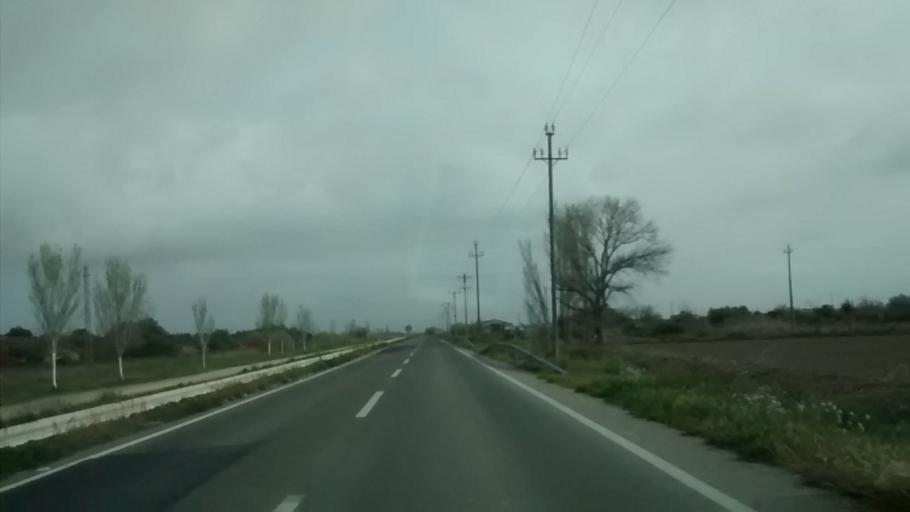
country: ES
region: Catalonia
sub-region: Provincia de Tarragona
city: Sant Carles de la Rapita
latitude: 40.6270
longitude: 0.6002
